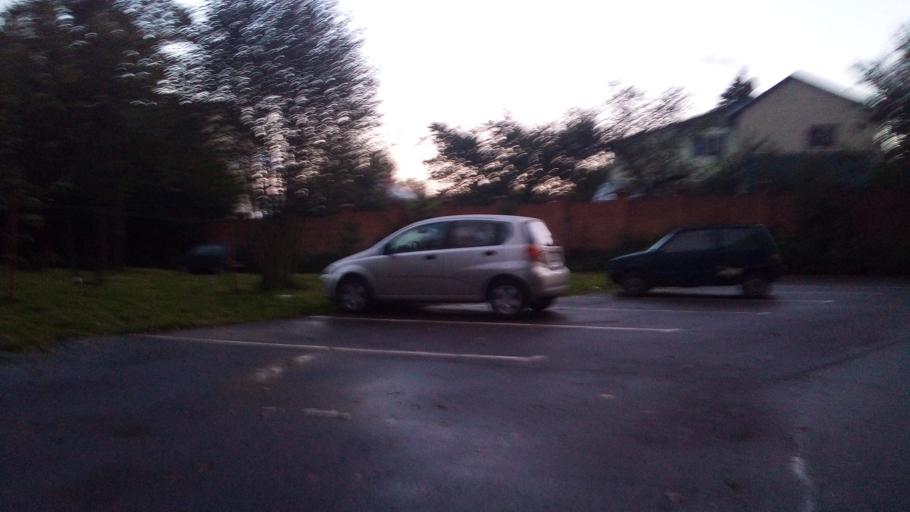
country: RU
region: Moskovskaya
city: Khot'kovo
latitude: 56.2461
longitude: 37.9418
